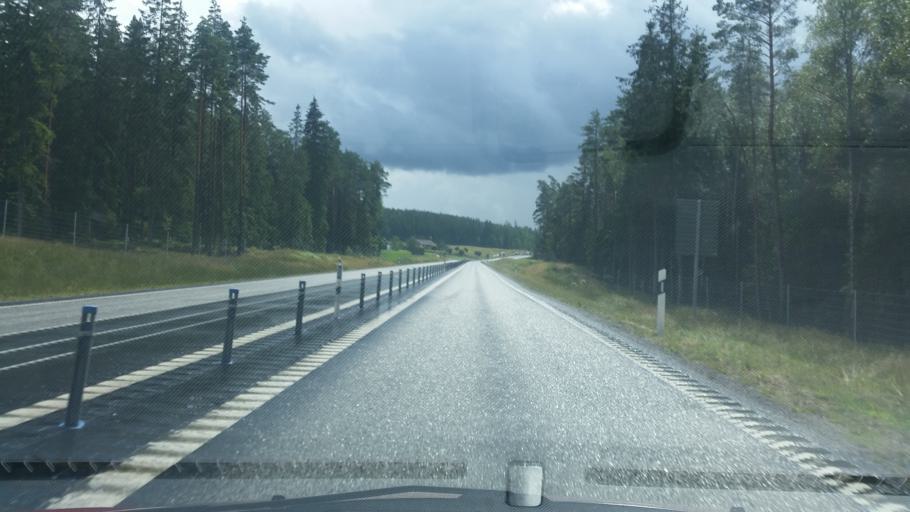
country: SE
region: Joenkoeping
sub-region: Gislaveds Kommun
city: Reftele
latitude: 57.2553
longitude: 13.6362
